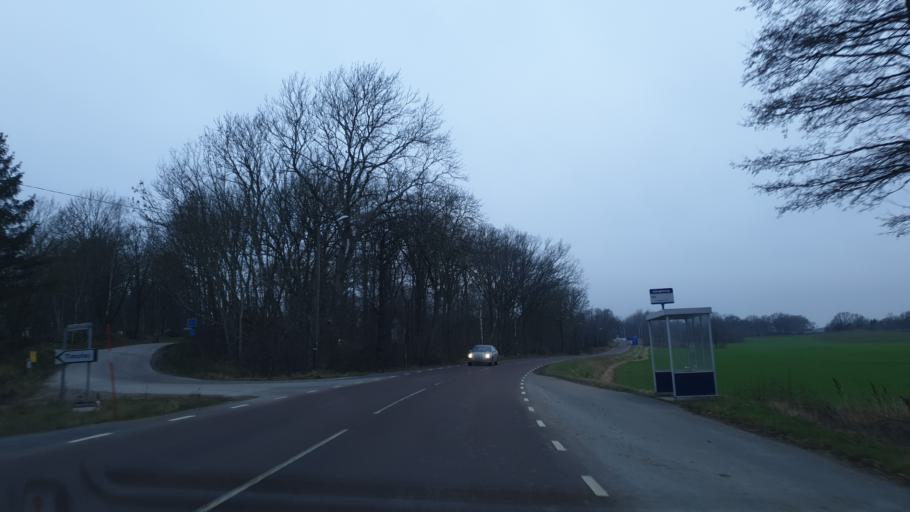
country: SE
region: Blekinge
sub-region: Karlskrona Kommun
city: Jaemjoe
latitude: 56.1676
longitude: 15.7470
